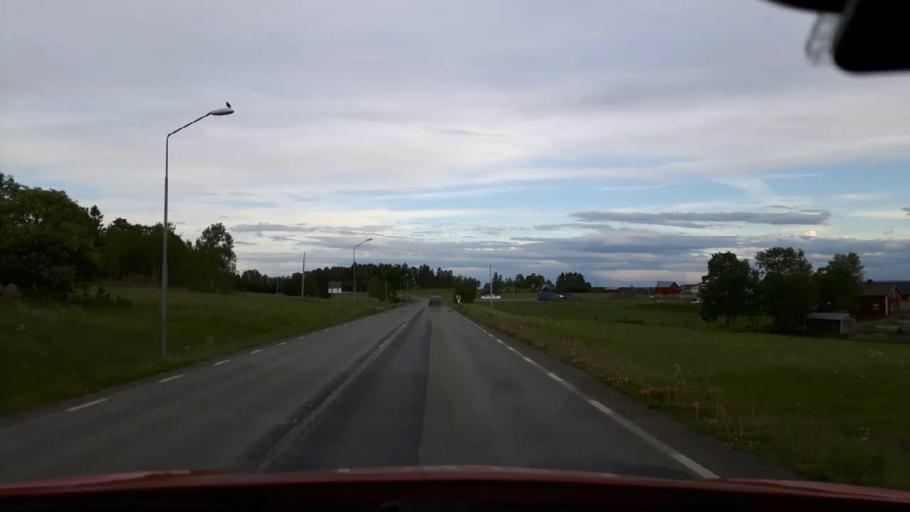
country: SE
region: Jaemtland
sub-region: OEstersunds Kommun
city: Ostersund
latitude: 63.1030
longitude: 14.4339
